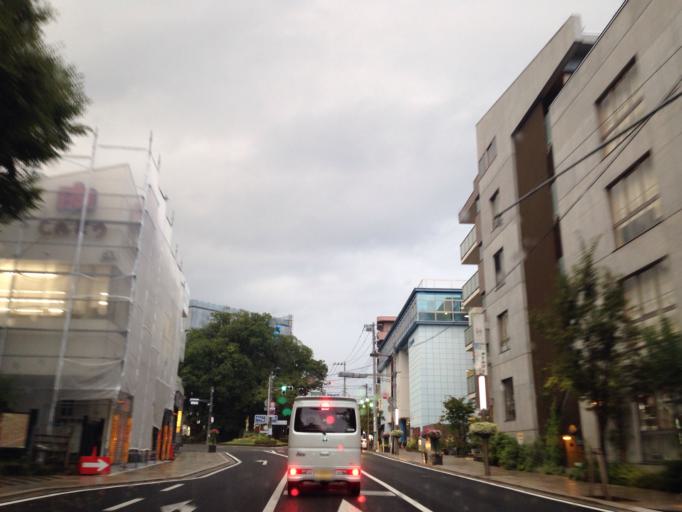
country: JP
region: Shizuoka
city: Mishima
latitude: 35.1232
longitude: 138.9140
